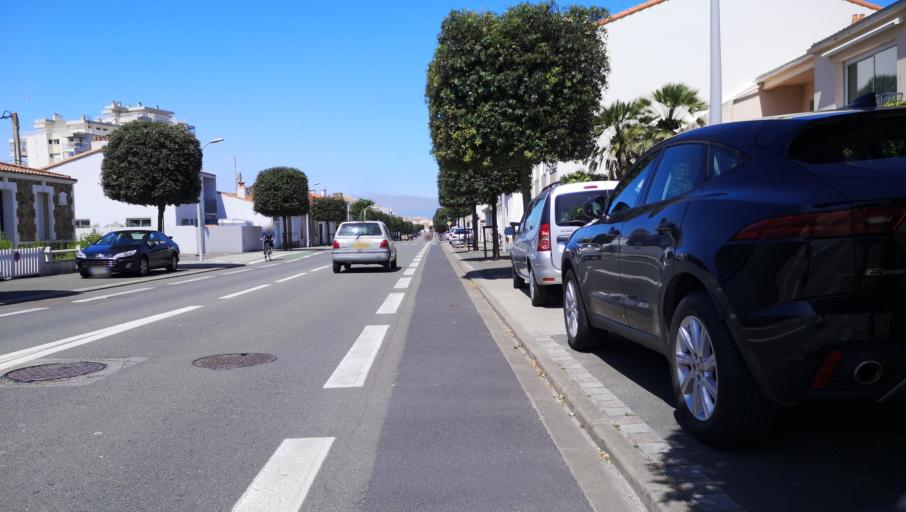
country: FR
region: Pays de la Loire
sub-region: Departement de la Vendee
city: Les Sables-d'Olonne
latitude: 46.4943
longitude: -1.7654
